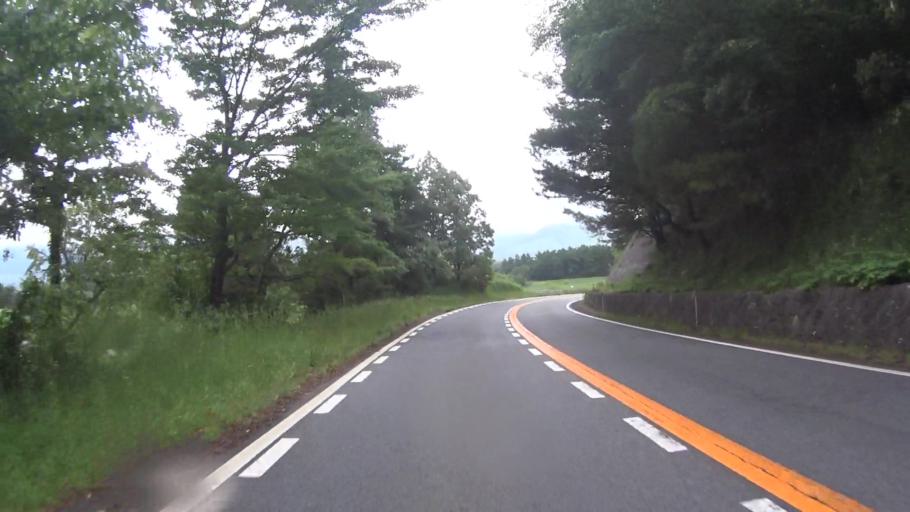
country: JP
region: Oita
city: Tsukawaki
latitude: 33.1632
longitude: 131.2421
